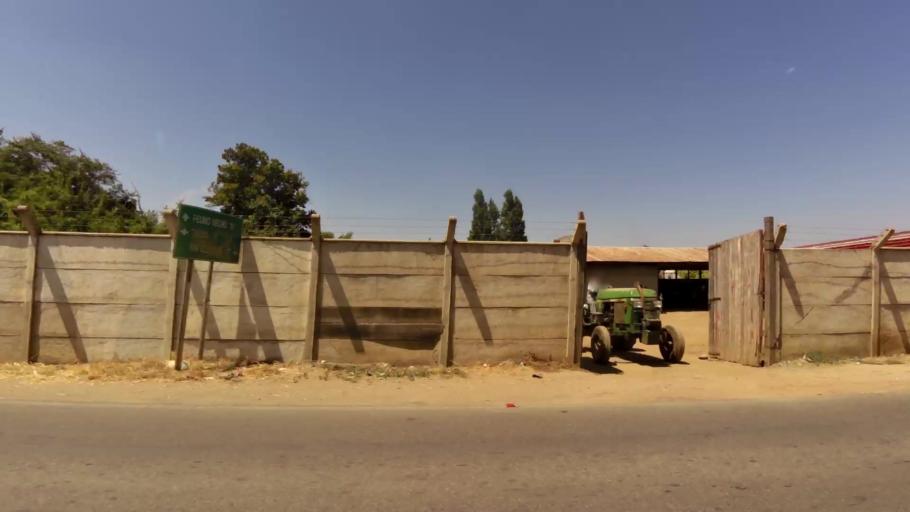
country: CL
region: Maule
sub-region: Provincia de Talca
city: Talca
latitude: -35.4403
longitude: -71.6137
